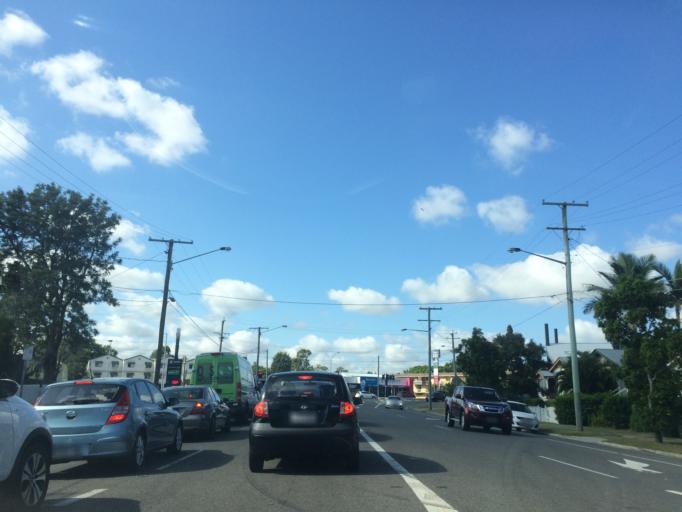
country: AU
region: Queensland
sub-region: Brisbane
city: Camp Hill
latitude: -27.4911
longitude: 153.0645
